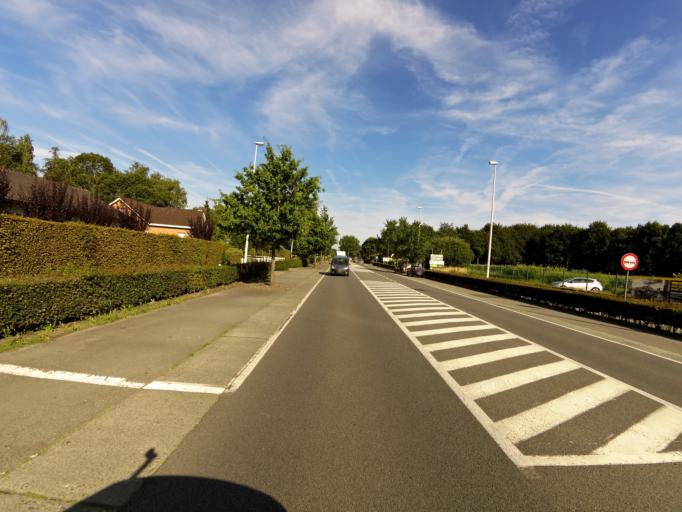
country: BE
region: Flanders
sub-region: Provincie West-Vlaanderen
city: Damme
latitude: 51.2048
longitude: 3.3056
